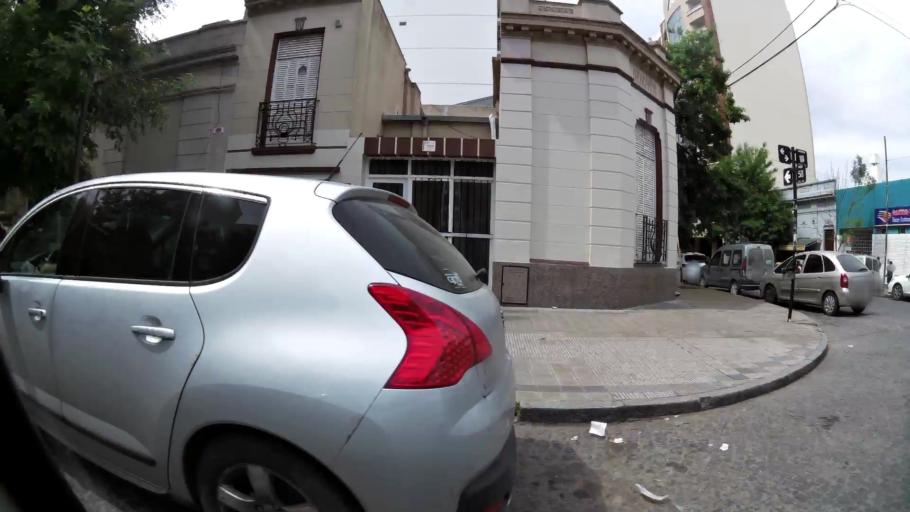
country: AR
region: Buenos Aires
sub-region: Partido de La Plata
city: La Plata
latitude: -34.9248
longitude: -57.9500
